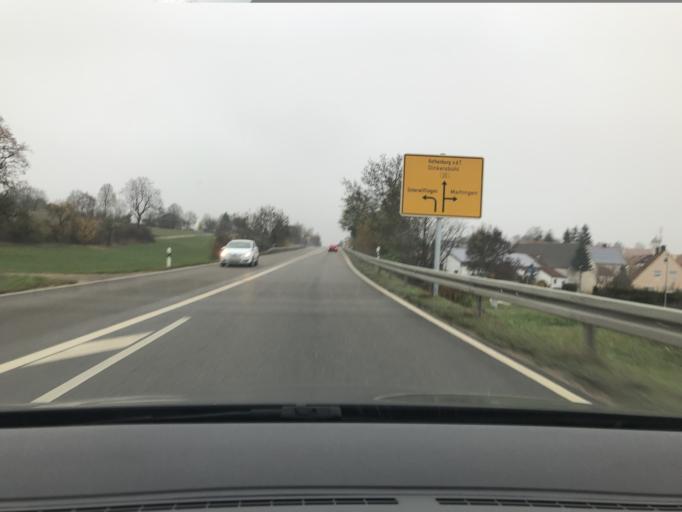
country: DE
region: Bavaria
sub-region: Swabia
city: Marktoffingen
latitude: 48.9213
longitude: 10.4659
